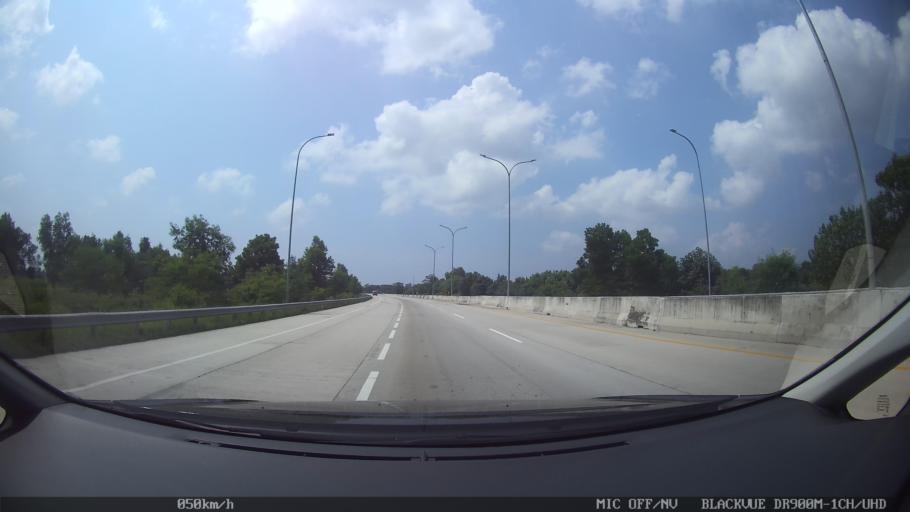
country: ID
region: Lampung
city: Natar
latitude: -5.2798
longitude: 105.2171
